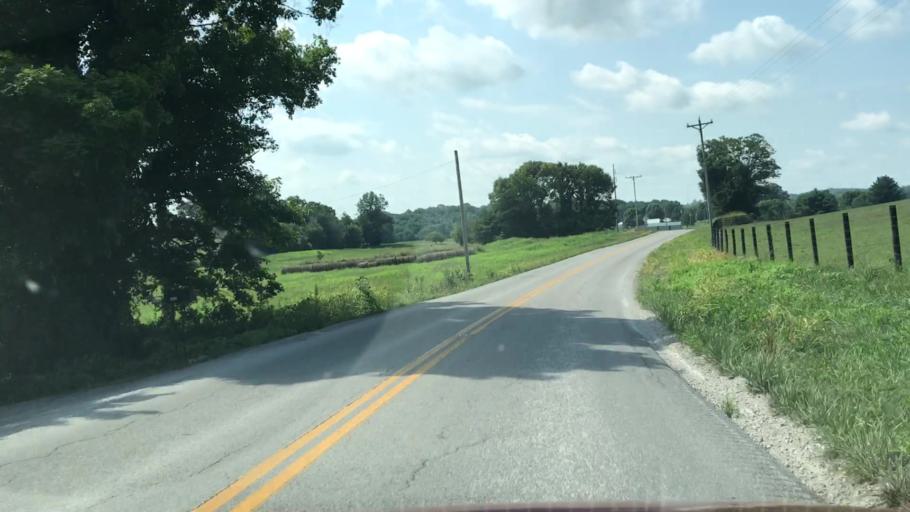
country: US
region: Kentucky
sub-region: Barren County
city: Glasgow
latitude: 36.8370
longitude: -85.8282
